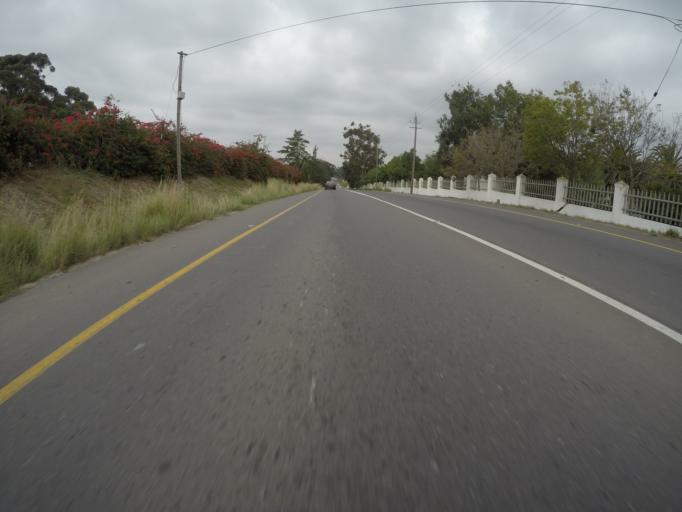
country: ZA
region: Western Cape
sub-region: City of Cape Town
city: Kraaifontein
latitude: -33.8404
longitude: 18.6086
